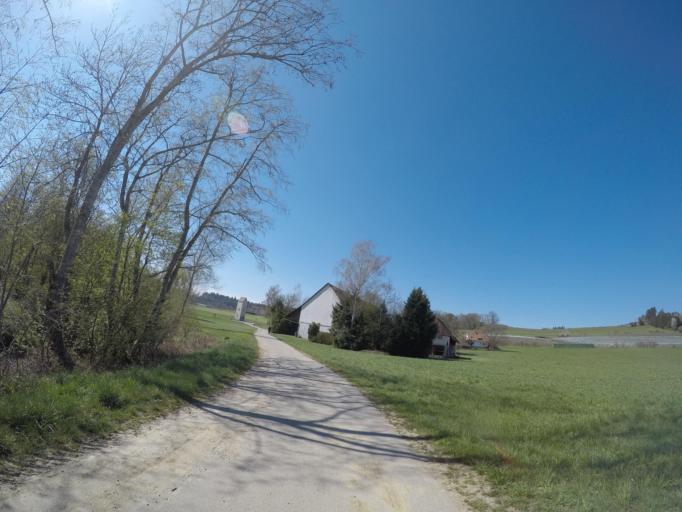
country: DE
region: Baden-Wuerttemberg
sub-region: Tuebingen Region
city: Horgenzell
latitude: 47.8245
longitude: 9.4572
